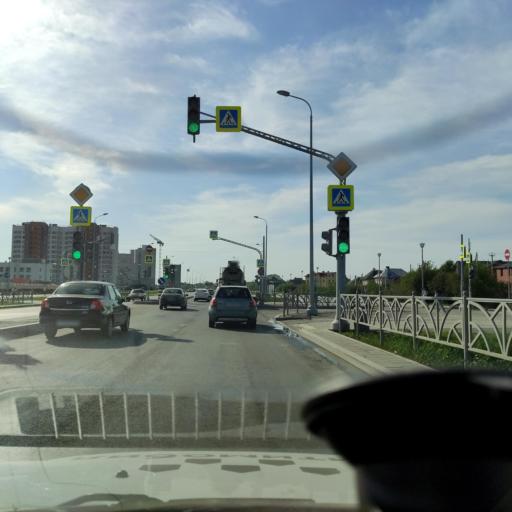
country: RU
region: Sverdlovsk
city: Shirokaya Rechka
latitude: 56.8001
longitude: 60.5071
